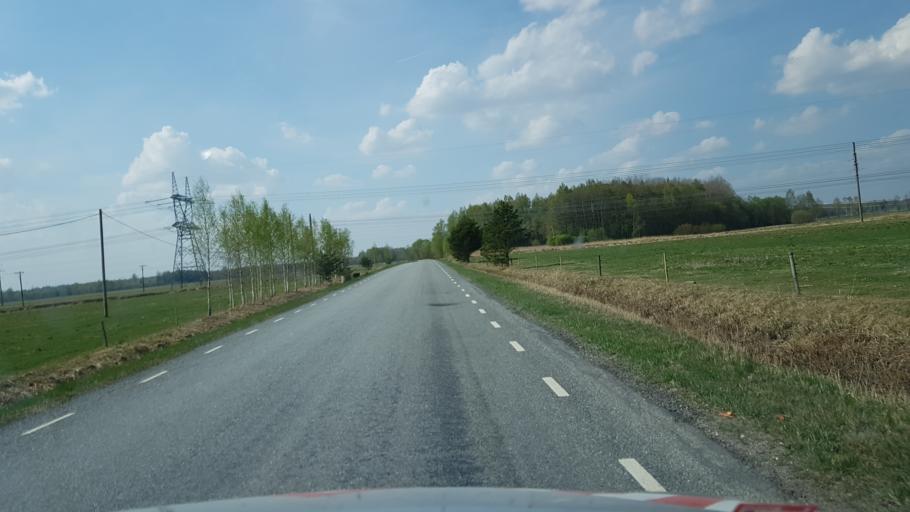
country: EE
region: Paernumaa
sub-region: Sindi linn
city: Sindi
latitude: 58.4300
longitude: 24.6425
